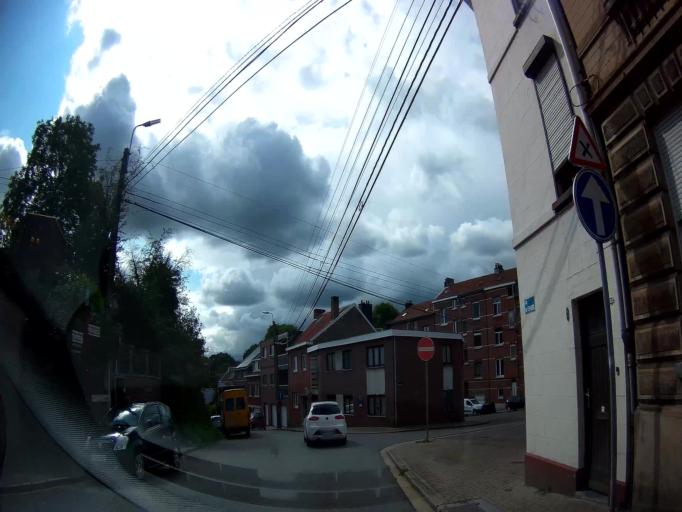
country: BE
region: Wallonia
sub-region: Province de Liege
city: Verviers
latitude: 50.6016
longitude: 5.8633
